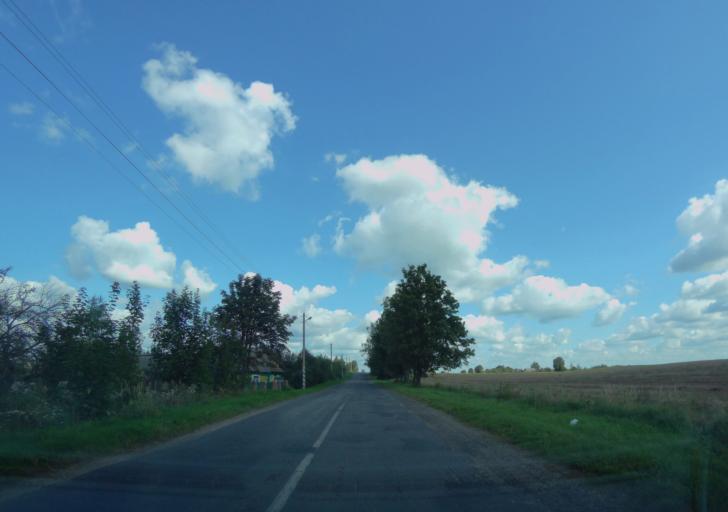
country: BY
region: Minsk
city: Zyembin
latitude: 54.4064
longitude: 28.4025
